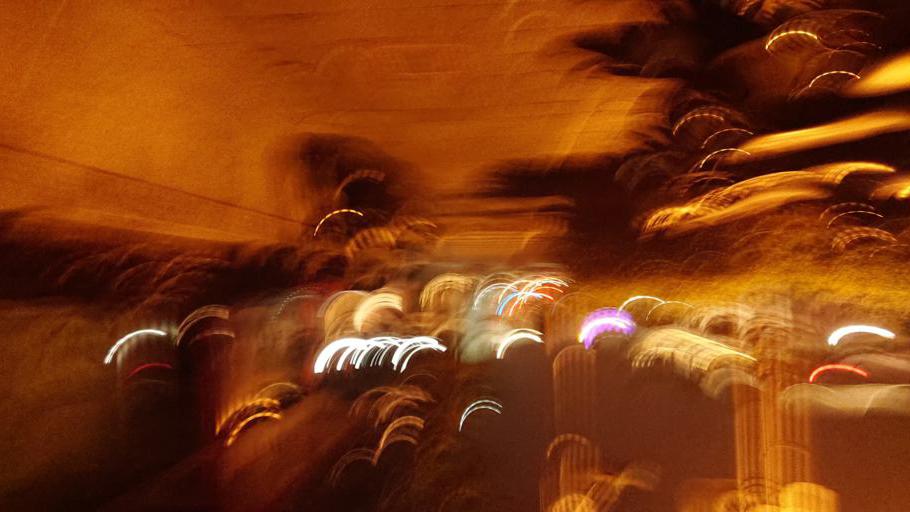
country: TW
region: Taiwan
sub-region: Tainan
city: Tainan
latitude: 22.9905
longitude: 120.2049
